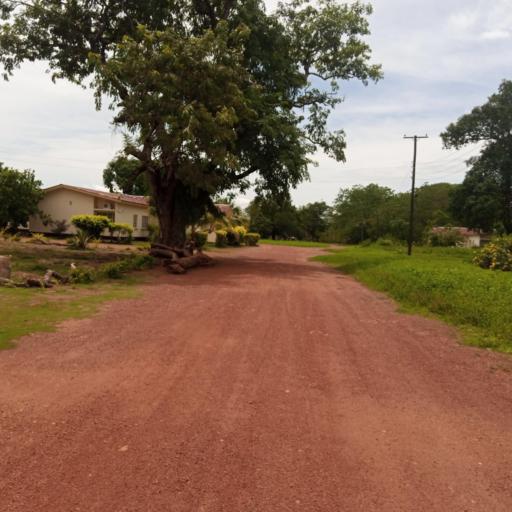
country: SL
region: Southern Province
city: Largo
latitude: 8.1108
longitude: -12.0786
